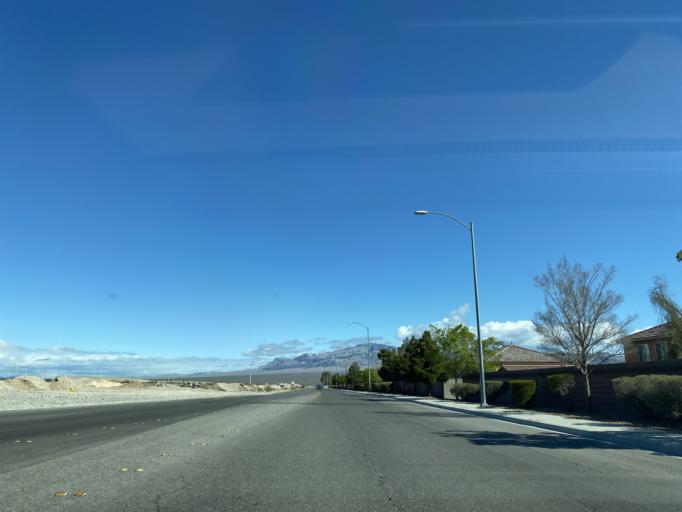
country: US
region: Nevada
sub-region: Clark County
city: Summerlin South
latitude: 36.3220
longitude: -115.2967
